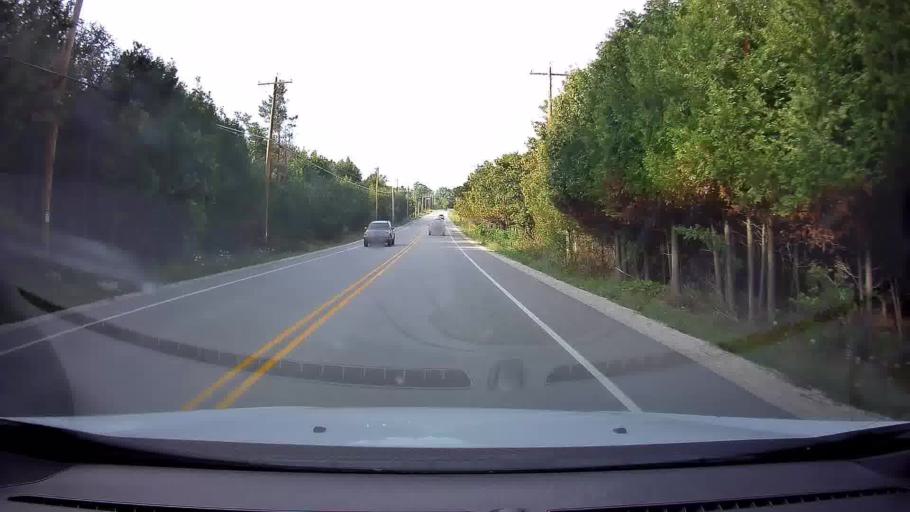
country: US
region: Wisconsin
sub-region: Door County
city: Sturgeon Bay
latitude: 45.1658
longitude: -87.1324
